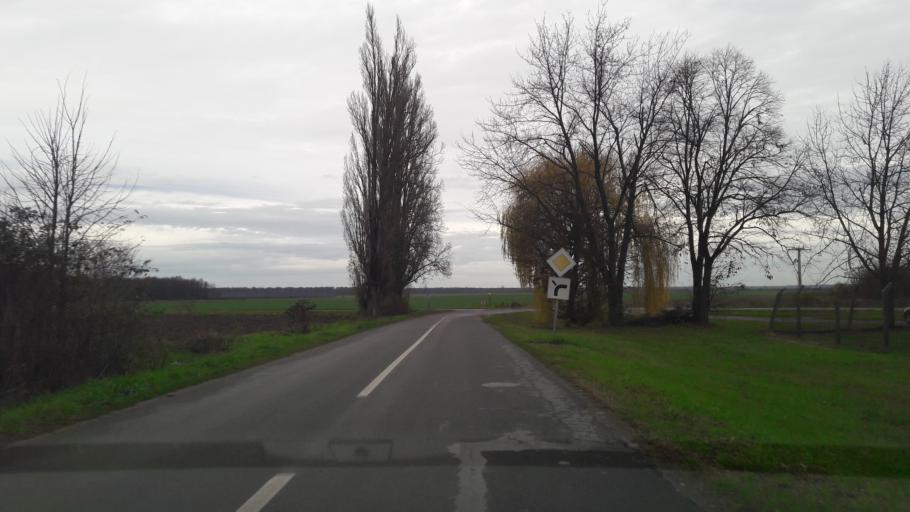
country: HR
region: Virovitick-Podravska
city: Zdenci
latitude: 45.6061
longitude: 18.0004
